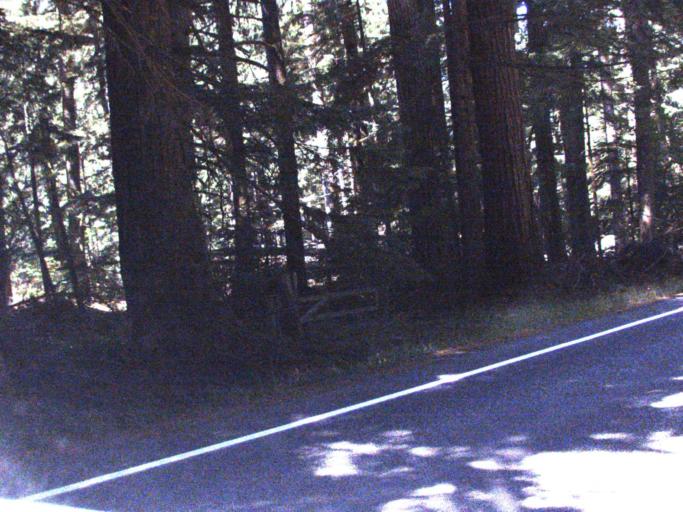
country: US
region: Washington
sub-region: King County
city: Enumclaw
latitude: 47.1573
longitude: -121.7253
